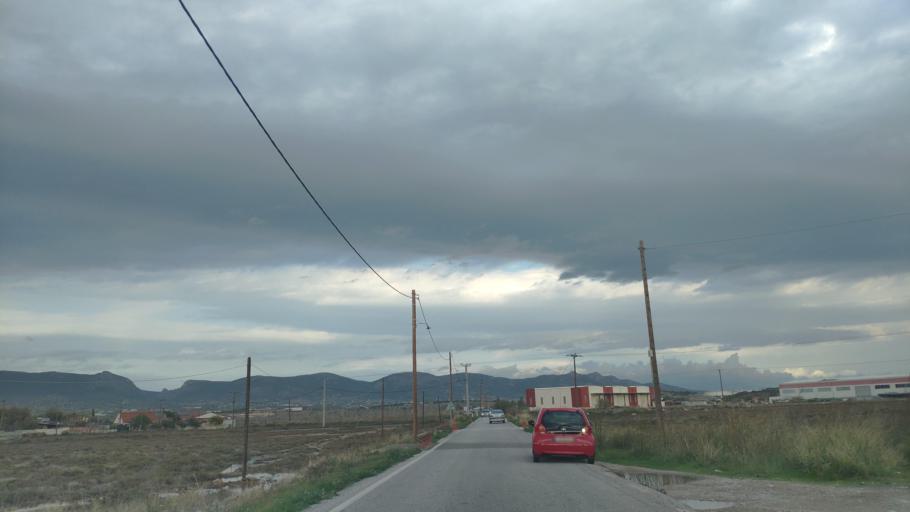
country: GR
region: Attica
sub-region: Nomarchia Dytikis Attikis
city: Megara
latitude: 37.9818
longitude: 23.3837
